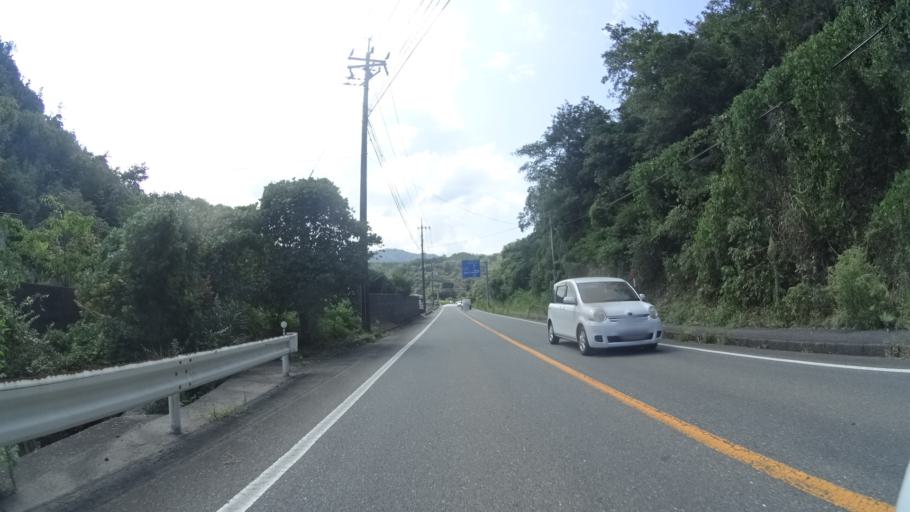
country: JP
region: Shimane
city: Masuda
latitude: 34.6248
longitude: 131.6131
